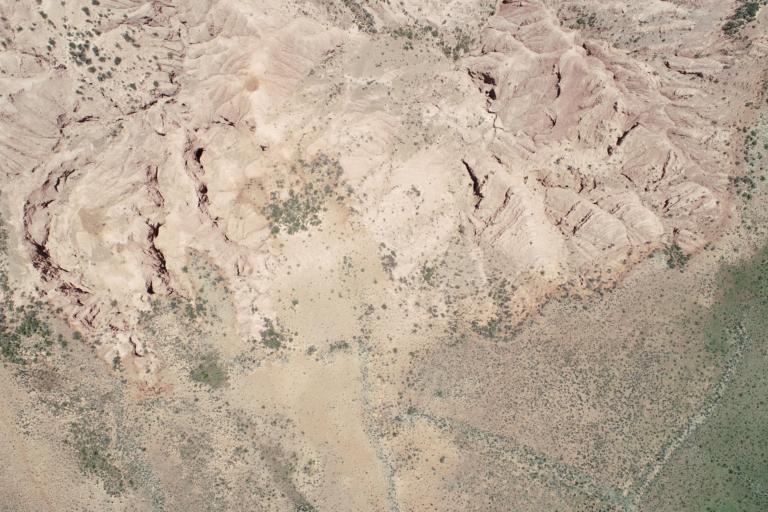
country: BO
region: La Paz
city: Curahuara de Carangas
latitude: -17.3055
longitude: -68.5007
